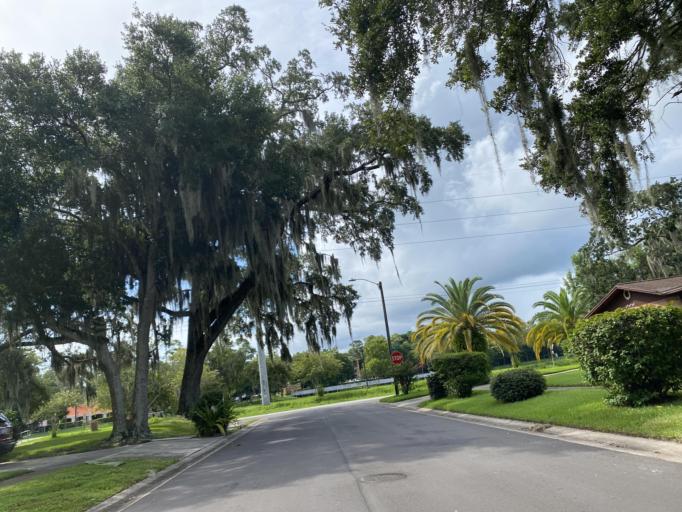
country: US
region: Florida
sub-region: Volusia County
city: Port Orange
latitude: 29.1330
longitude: -81.0040
